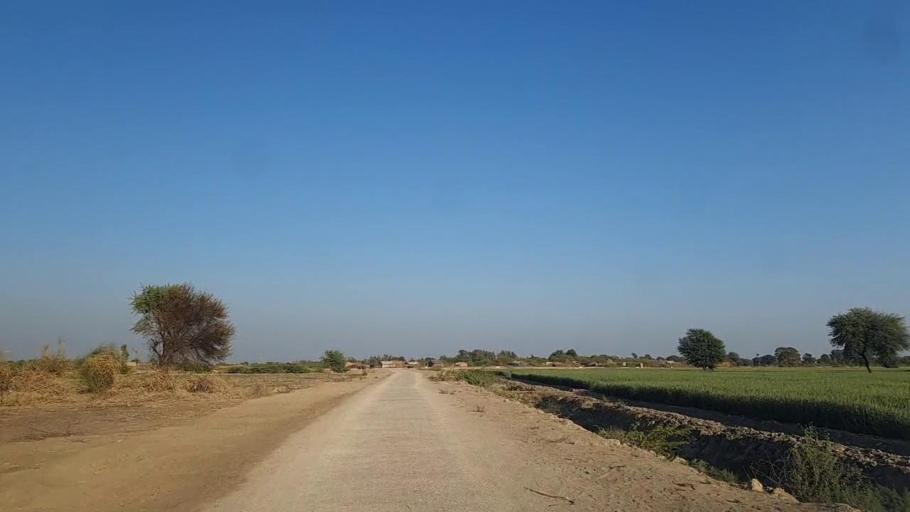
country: PK
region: Sindh
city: Samaro
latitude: 25.3468
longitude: 69.4268
